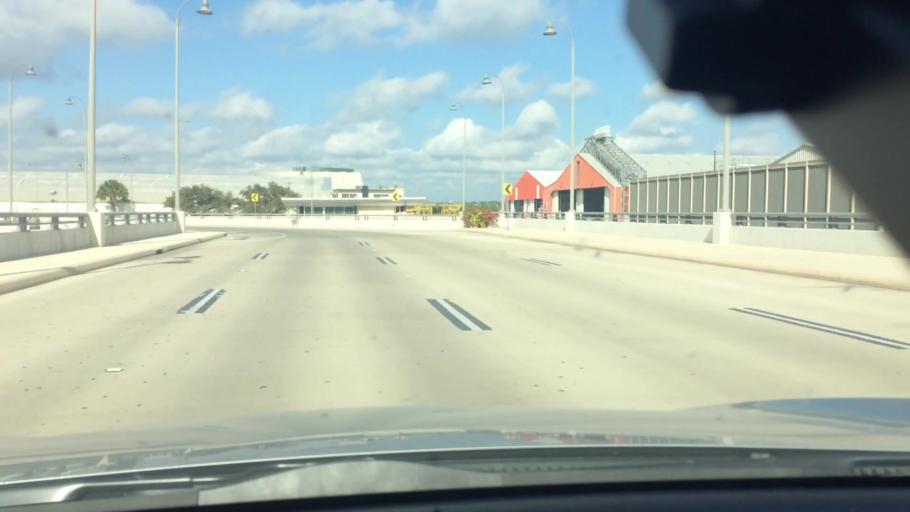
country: US
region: Texas
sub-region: Bexar County
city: Castle Hills
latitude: 29.5281
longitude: -98.4759
